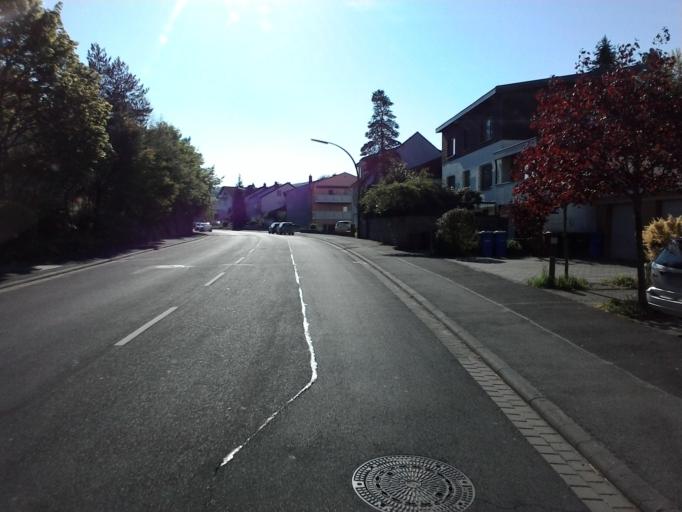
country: DE
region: Bavaria
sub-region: Regierungsbezirk Unterfranken
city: Marktheidenfeld
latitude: 49.8386
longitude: 9.5994
